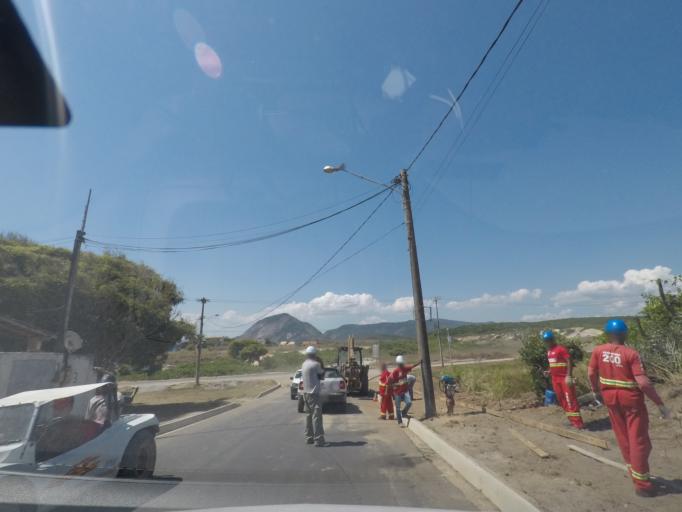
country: BR
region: Rio de Janeiro
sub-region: Marica
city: Marica
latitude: -22.9699
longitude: -42.9038
